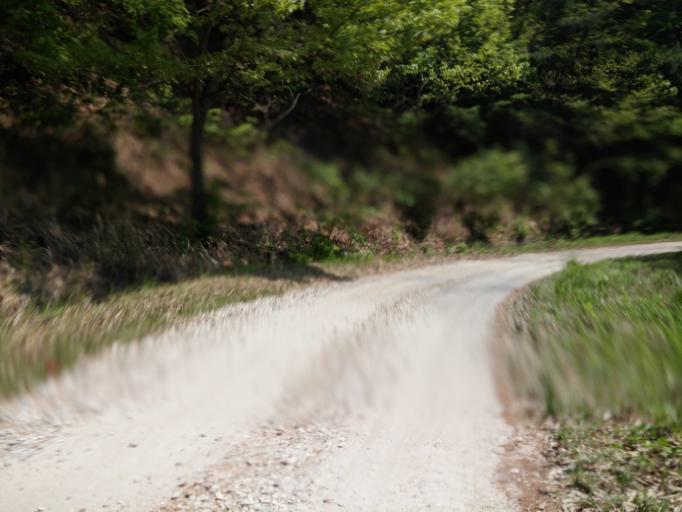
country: KR
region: Chungcheongbuk-do
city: Okcheon
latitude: 36.4194
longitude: 127.5946
